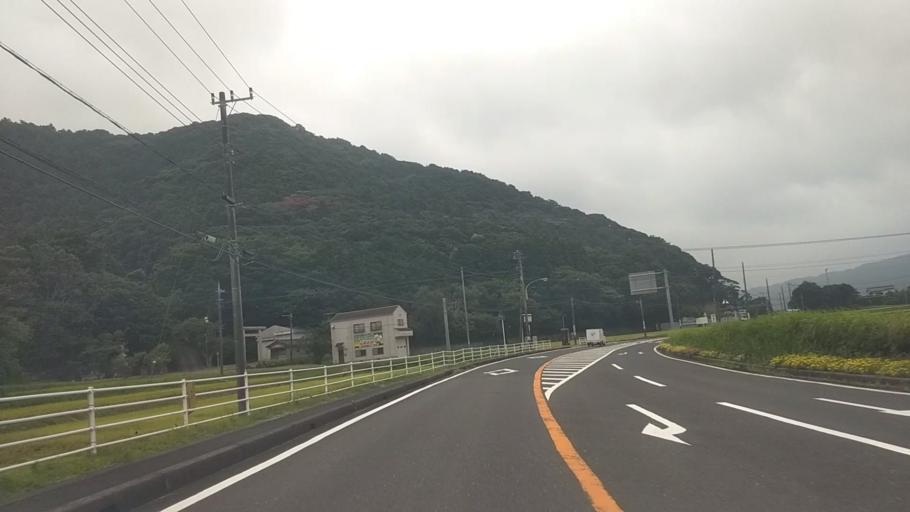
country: JP
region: Chiba
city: Kawaguchi
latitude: 35.1324
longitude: 140.0787
